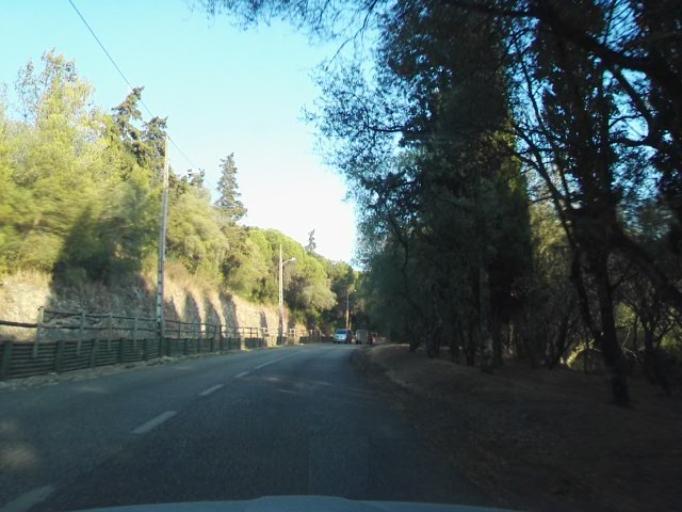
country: PT
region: Lisbon
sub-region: Oeiras
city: Alges
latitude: 38.7273
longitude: -9.2010
